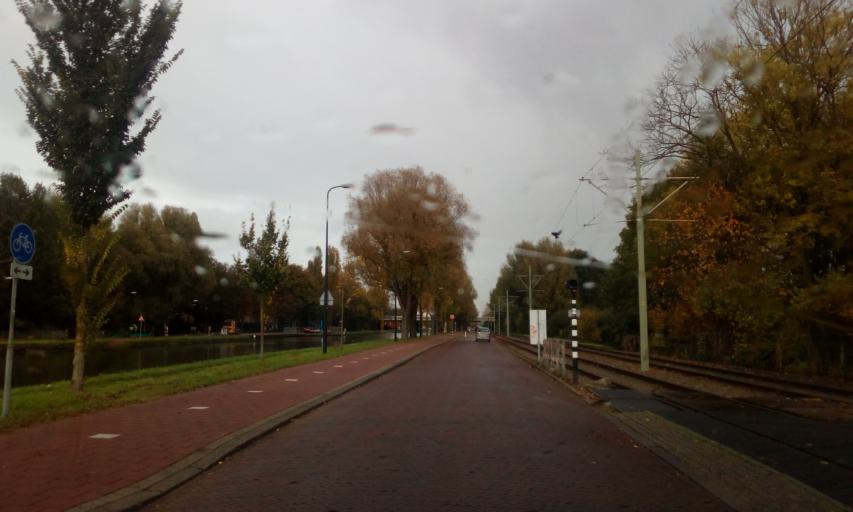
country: NL
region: South Holland
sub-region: Gemeente Rijswijk
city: Rijswijk
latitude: 52.0369
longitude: 4.3454
